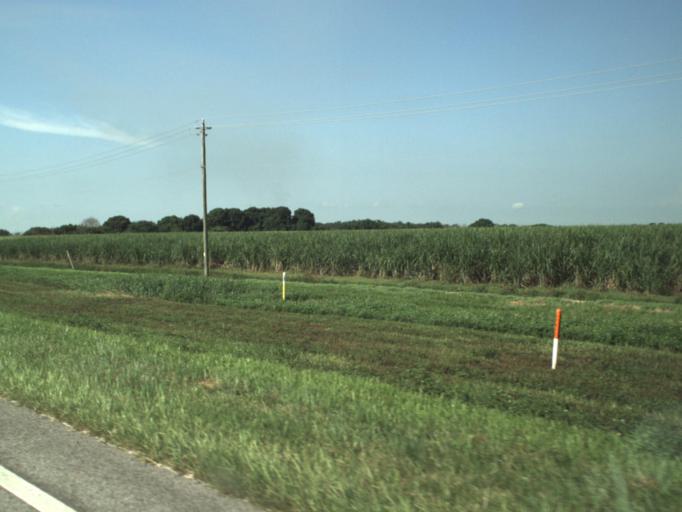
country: US
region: Florida
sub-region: Palm Beach County
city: South Bay
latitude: 26.6275
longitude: -80.7122
